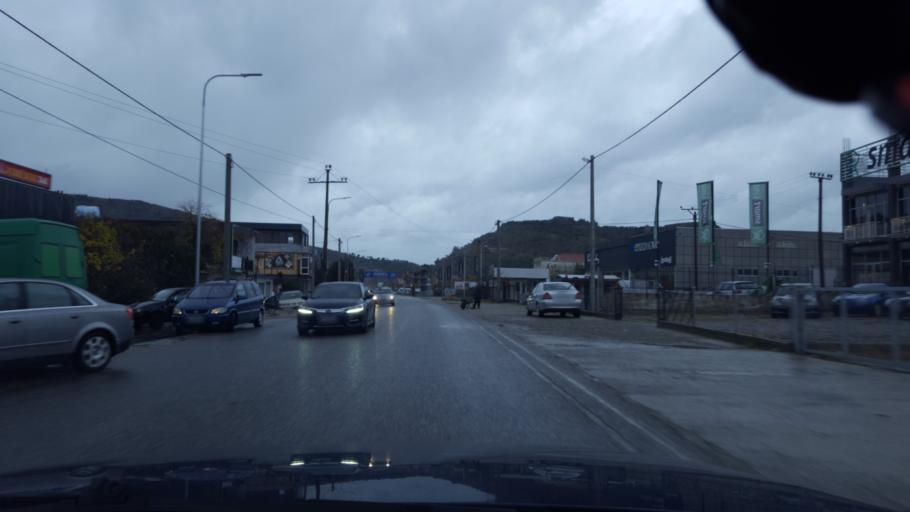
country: AL
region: Shkoder
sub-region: Rrethi i Malesia e Madhe
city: Kuc
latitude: 42.0373
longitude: 19.4983
